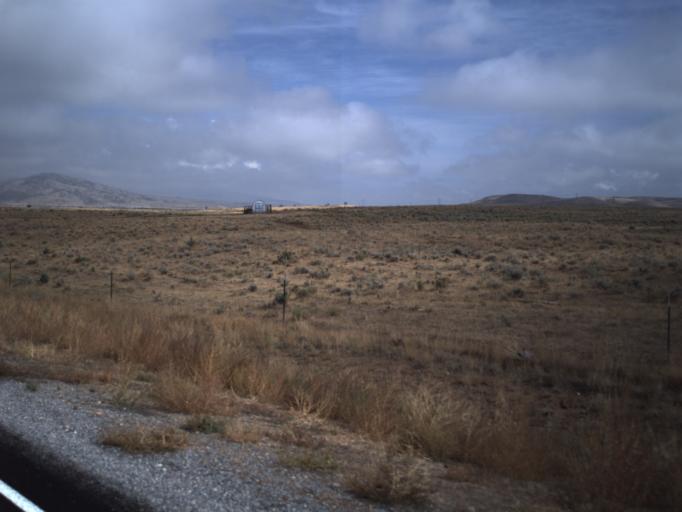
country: US
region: Utah
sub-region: Rich County
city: Randolph
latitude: 41.4902
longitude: -111.1190
